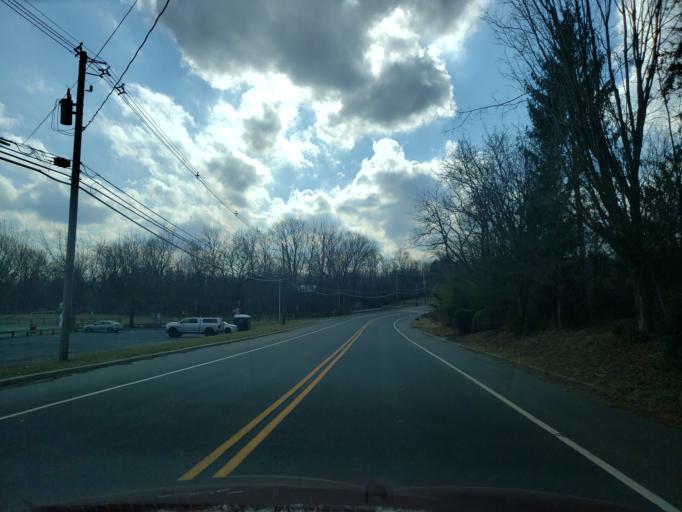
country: US
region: New Jersey
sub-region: Hunterdon County
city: Flemington
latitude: 40.4937
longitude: -74.8901
